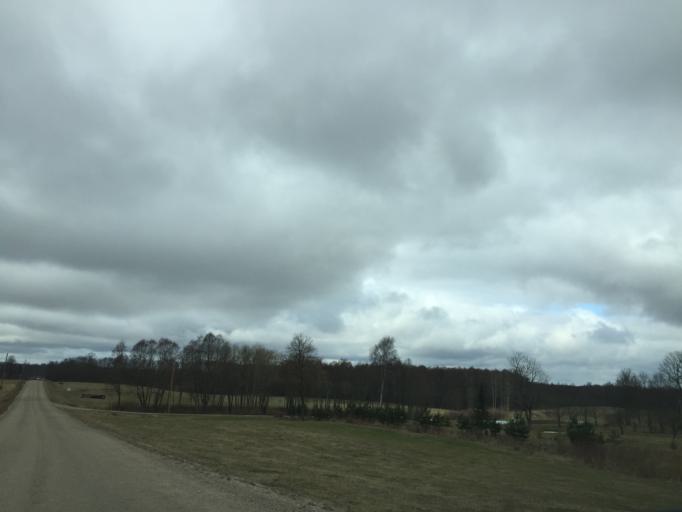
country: LV
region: Ilukste
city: Ilukste
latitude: 56.0575
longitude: 26.1750
